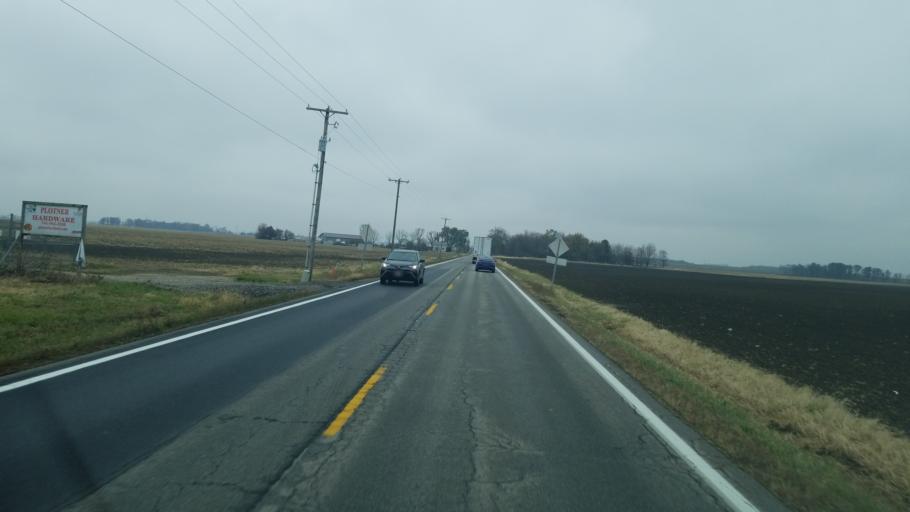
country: US
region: Ohio
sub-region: Union County
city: Richwood
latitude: 40.3965
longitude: -83.2684
